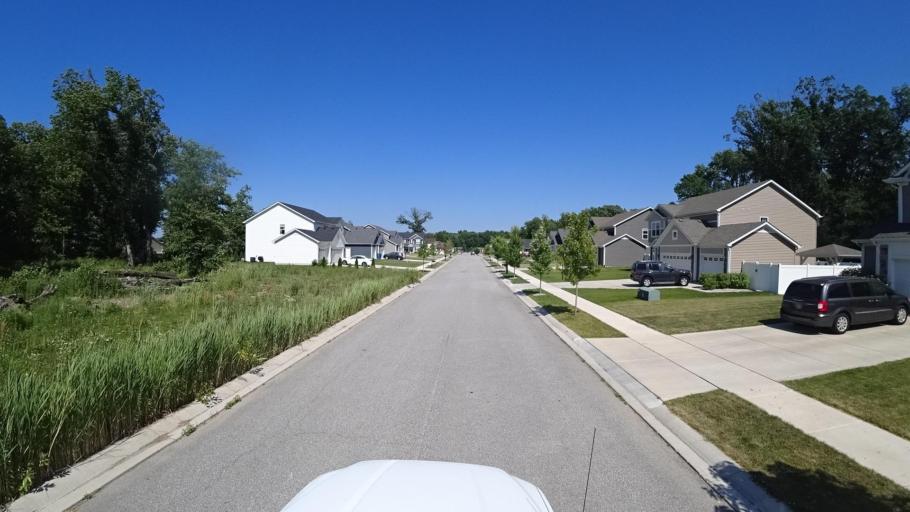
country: US
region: Indiana
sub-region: Porter County
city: Burns Harbor
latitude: 41.5997
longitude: -87.1124
